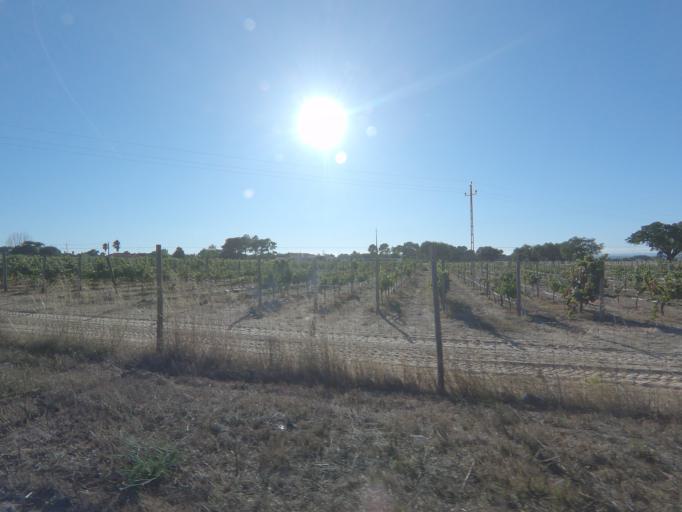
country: PT
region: Setubal
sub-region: Palmela
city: Quinta do Anjo
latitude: 38.5403
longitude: -8.9860
